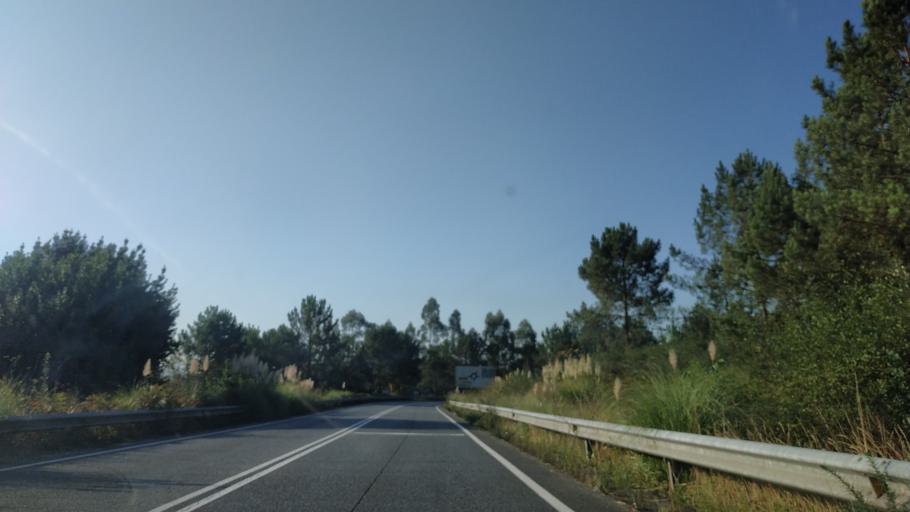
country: ES
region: Galicia
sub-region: Provincia da Coruna
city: Carballo
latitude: 43.2340
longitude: -8.6782
